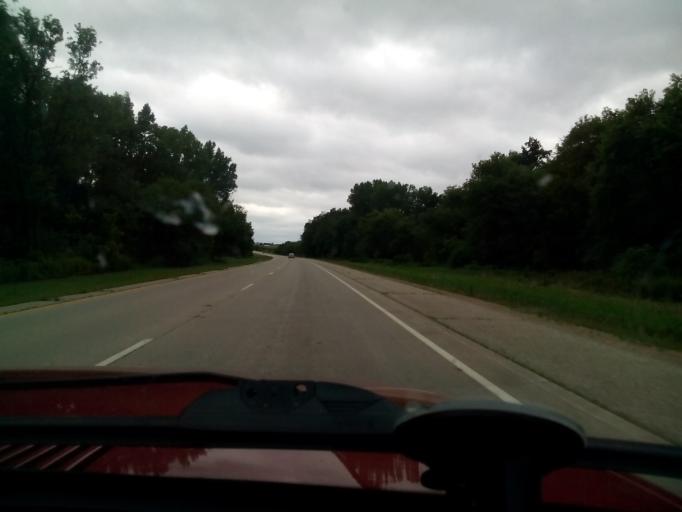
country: US
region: Wisconsin
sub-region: Dane County
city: Sun Prairie
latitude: 43.2296
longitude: -89.1581
